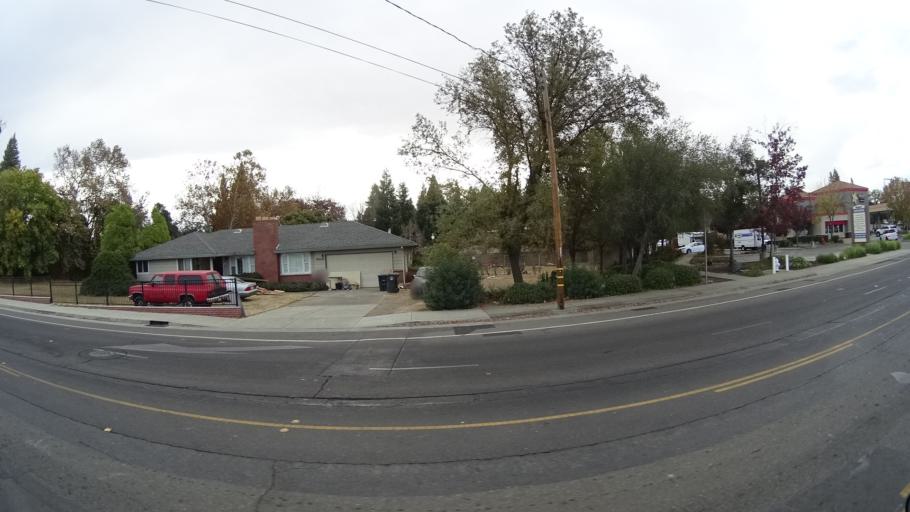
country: US
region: California
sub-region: Sacramento County
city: Citrus Heights
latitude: 38.7044
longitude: -121.2709
